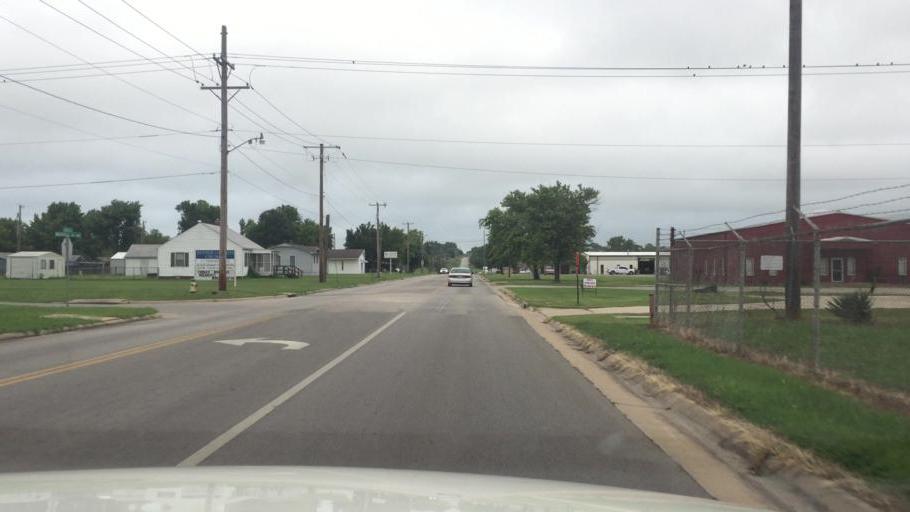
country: US
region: Kansas
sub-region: Montgomery County
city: Coffeyville
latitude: 37.0468
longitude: -95.6473
